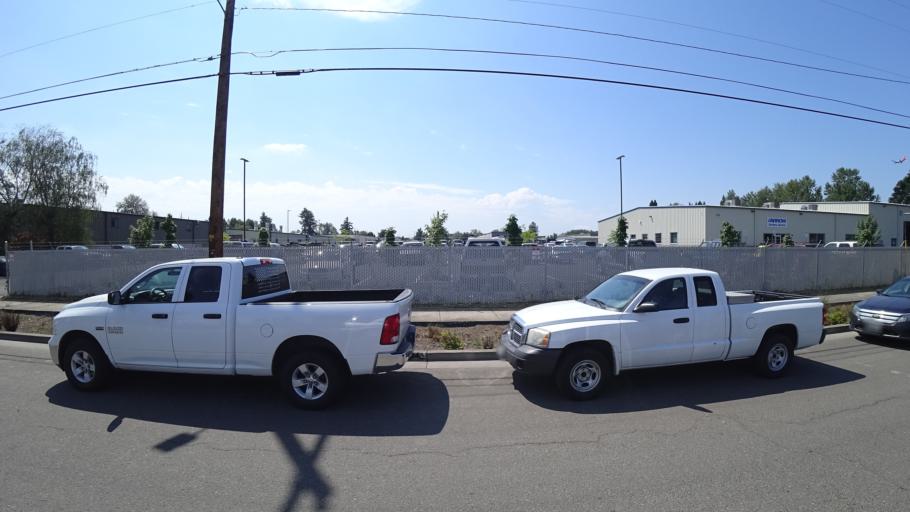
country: US
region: Oregon
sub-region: Multnomah County
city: Lents
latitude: 45.5626
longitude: -122.5507
